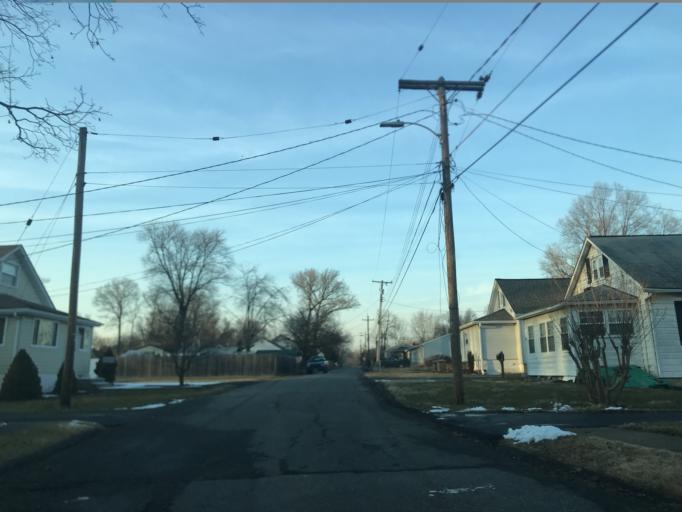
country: US
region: Maryland
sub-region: Harford County
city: Edgewood
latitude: 39.4182
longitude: -76.2912
